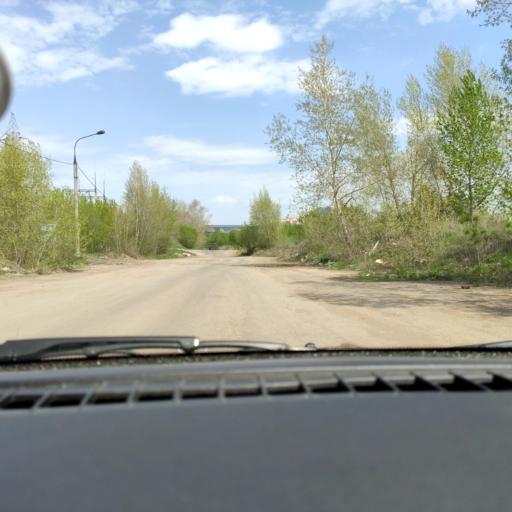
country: RU
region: Samara
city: Samara
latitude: 53.1770
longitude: 50.1240
